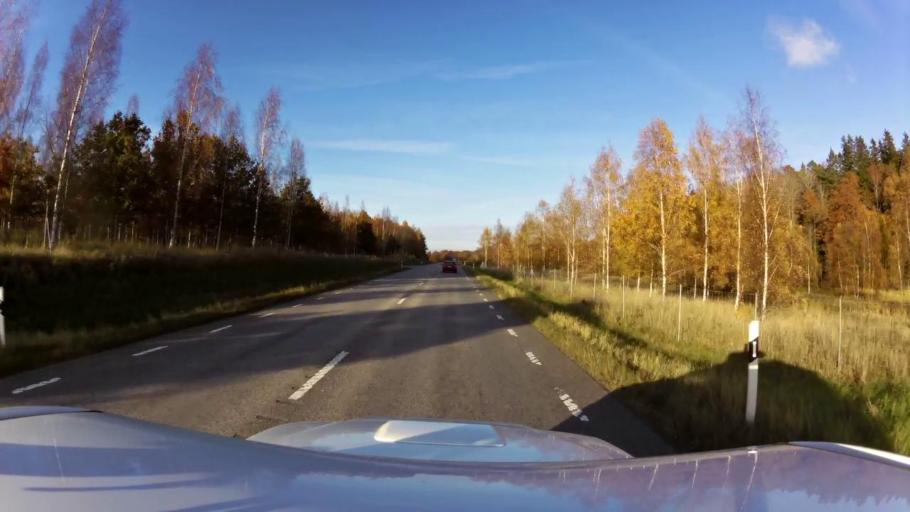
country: SE
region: OEstergoetland
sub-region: Kinda Kommun
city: Rimforsa
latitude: 58.2042
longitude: 15.6685
